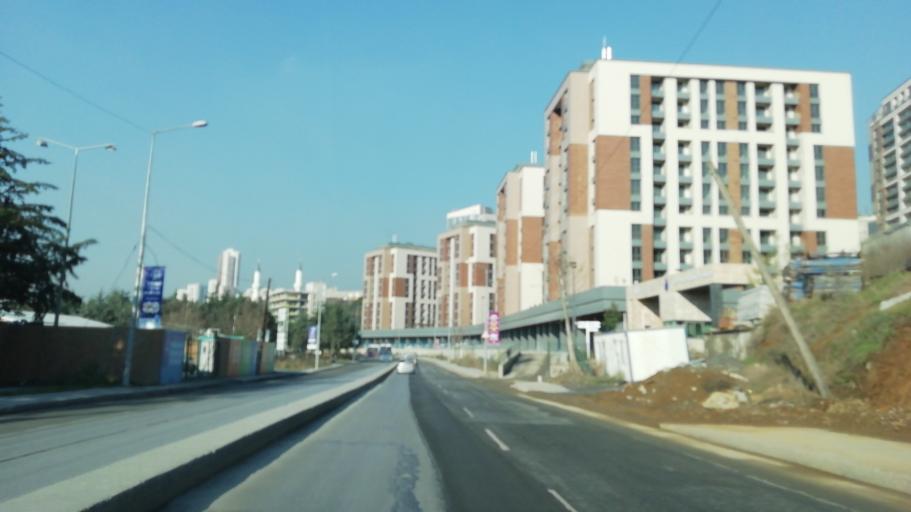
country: TR
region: Istanbul
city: Sisli
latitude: 41.0867
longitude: 28.9504
